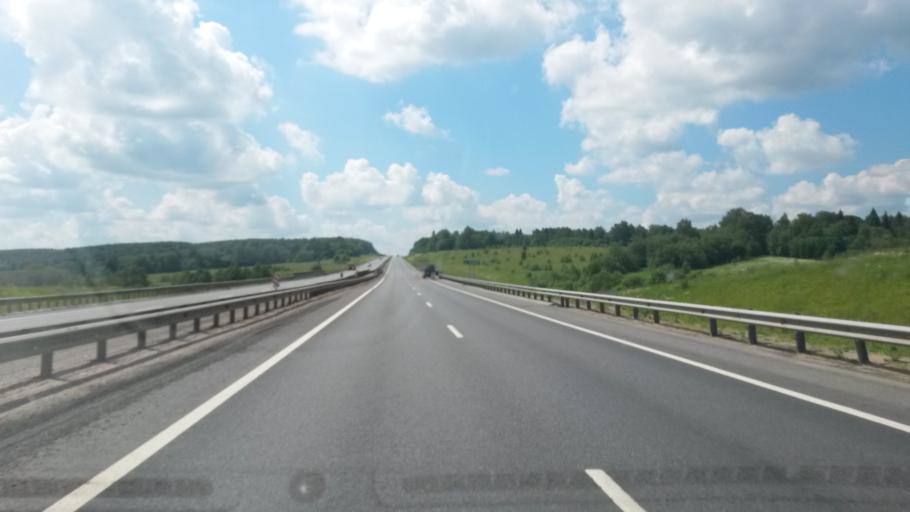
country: RU
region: Vladimir
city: Strunino
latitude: 56.5369
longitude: 38.5836
